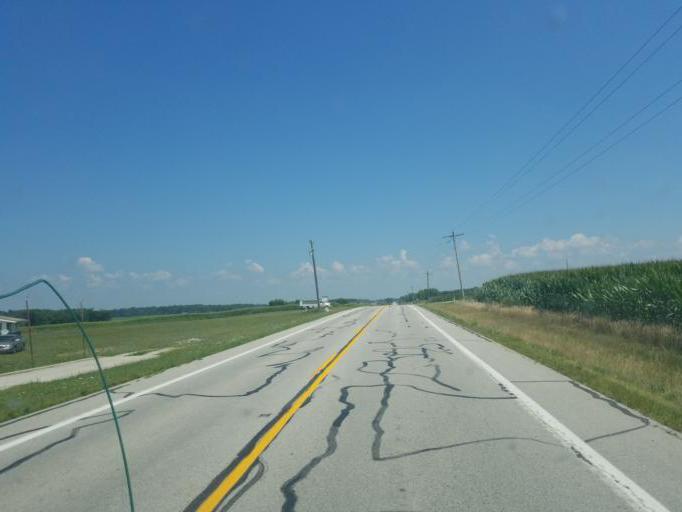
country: US
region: Ohio
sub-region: Shelby County
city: Anna
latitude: 40.3952
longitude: -84.1536
